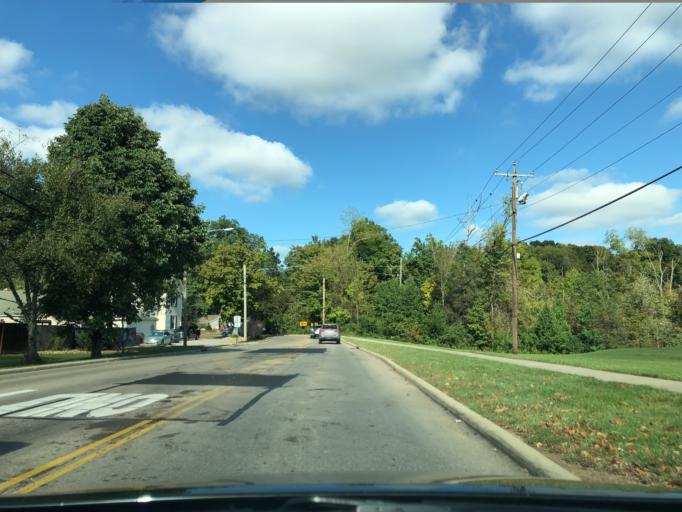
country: US
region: Ohio
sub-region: Hamilton County
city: Loveland
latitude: 39.2588
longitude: -84.2494
